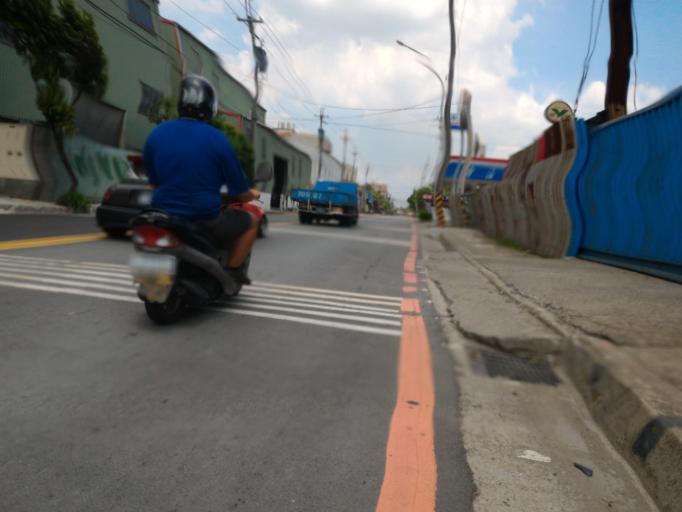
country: TW
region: Taipei
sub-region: Taipei
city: Banqiao
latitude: 24.9714
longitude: 121.4151
